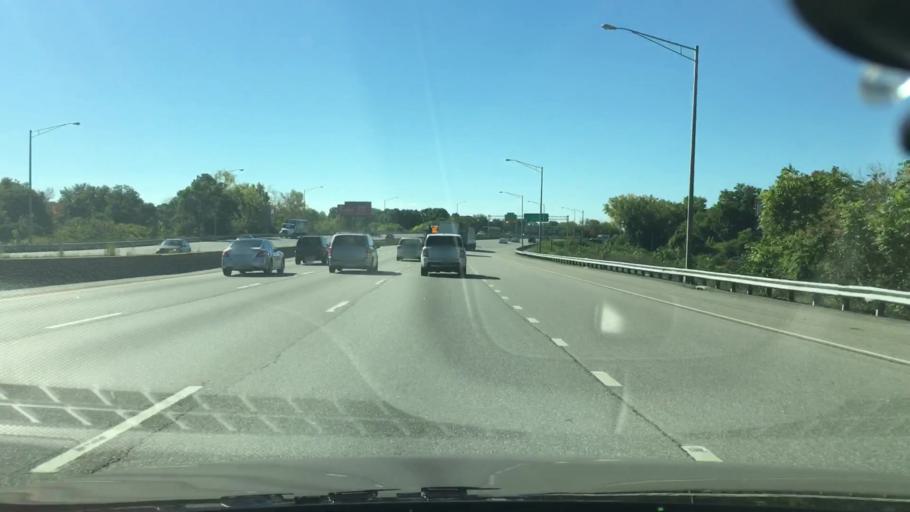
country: US
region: Connecticut
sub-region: Hartford County
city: Hartford
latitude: 41.7563
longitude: -72.7010
